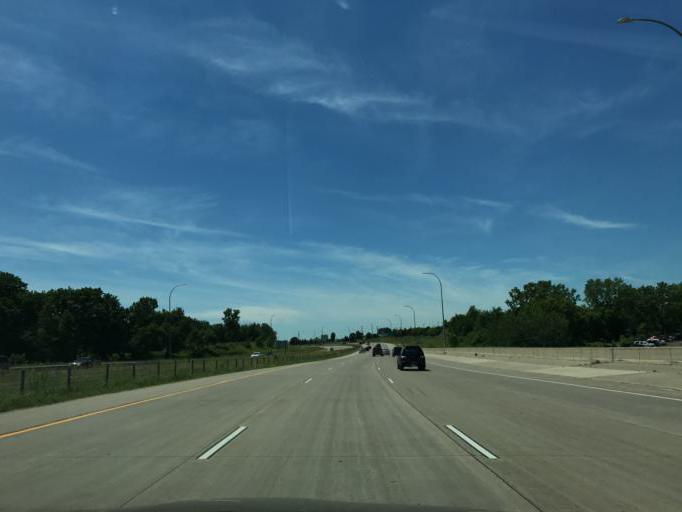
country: US
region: Minnesota
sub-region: Hennepin County
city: Osseo
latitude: 45.1047
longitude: -93.3952
